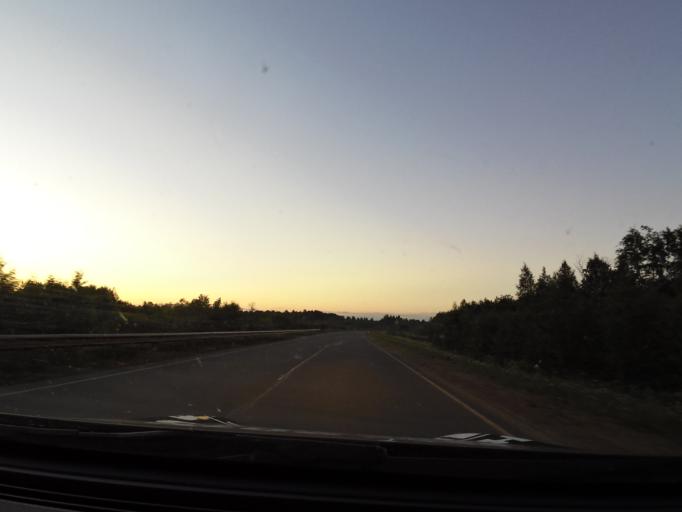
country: RU
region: Vologda
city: Vytegra
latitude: 60.9850
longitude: 36.1062
